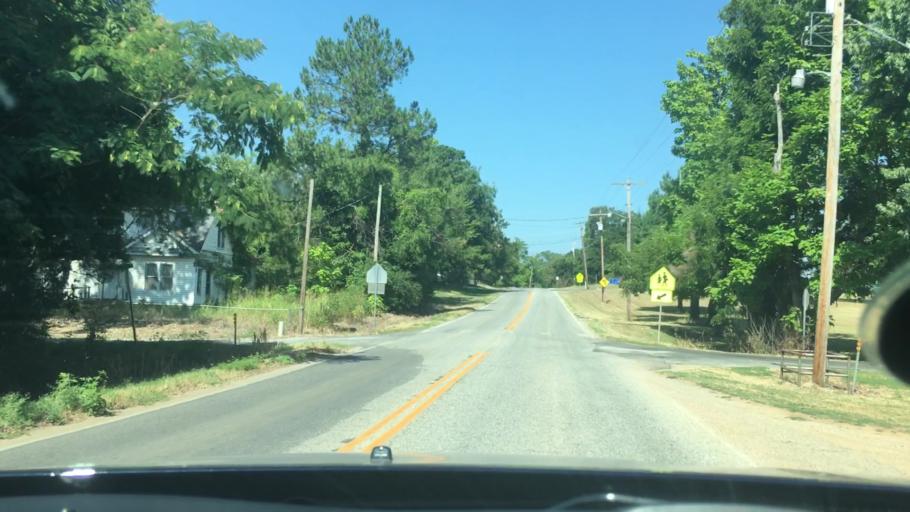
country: US
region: Oklahoma
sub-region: Johnston County
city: Tishomingo
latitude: 34.2404
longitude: -96.5522
